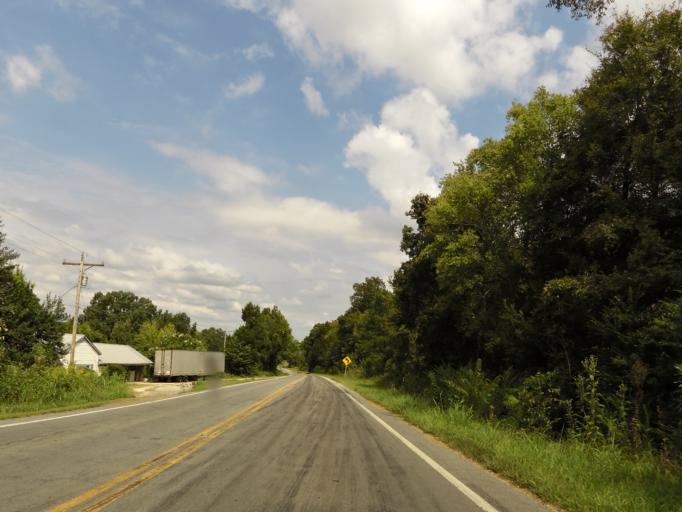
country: US
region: Tennessee
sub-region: Decatur County
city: Decaturville
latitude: 35.6185
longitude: -88.0182
